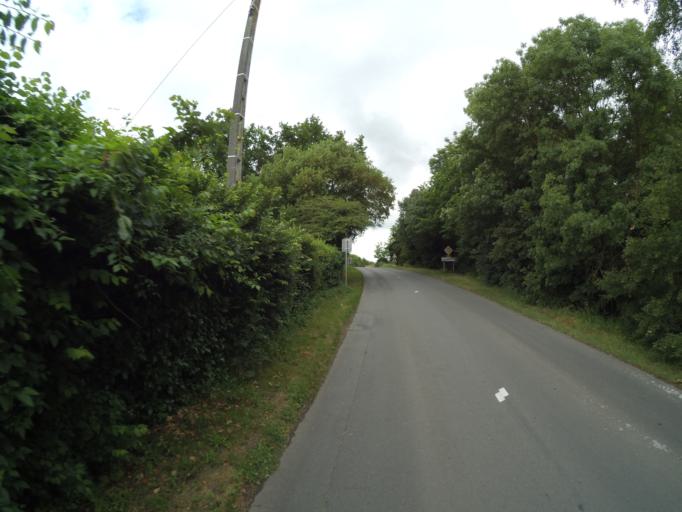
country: FR
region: Poitou-Charentes
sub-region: Departement de la Charente-Maritime
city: Breuil-Magne
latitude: 45.9639
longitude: -0.9700
